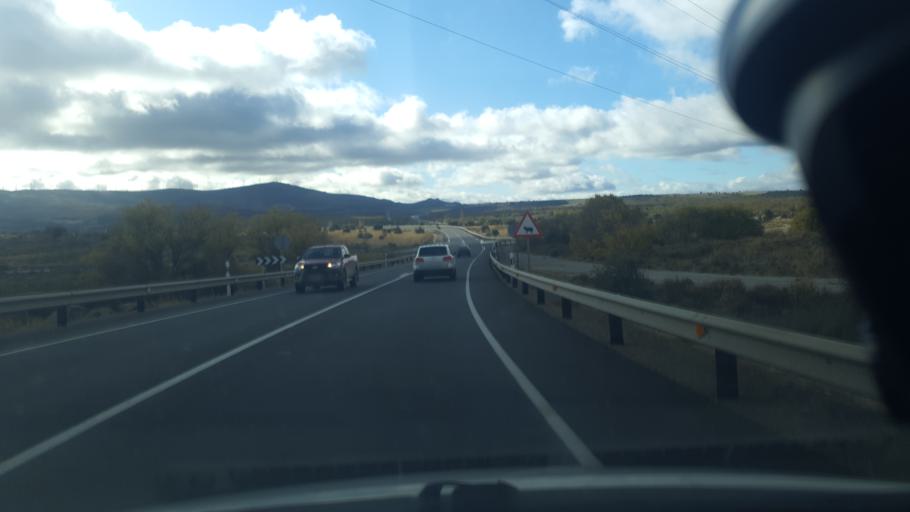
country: ES
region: Castille and Leon
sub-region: Provincia de Segovia
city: Villacastin
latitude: 40.7676
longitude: -4.4296
